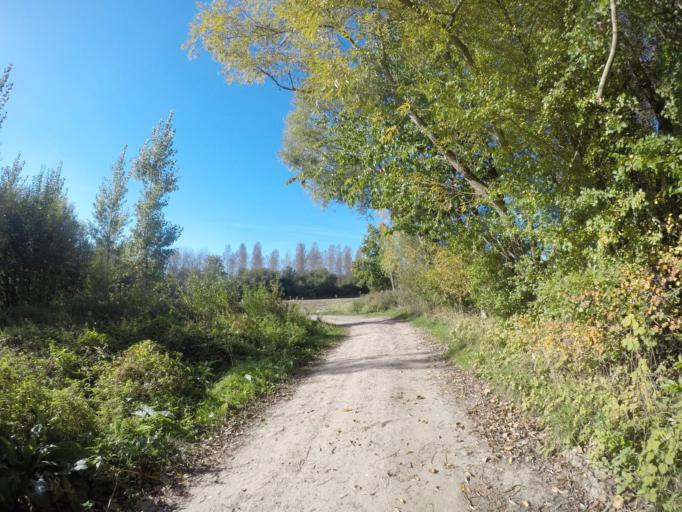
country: BE
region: Flanders
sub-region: Provincie Limburg
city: Alken
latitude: 50.8659
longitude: 5.3194
